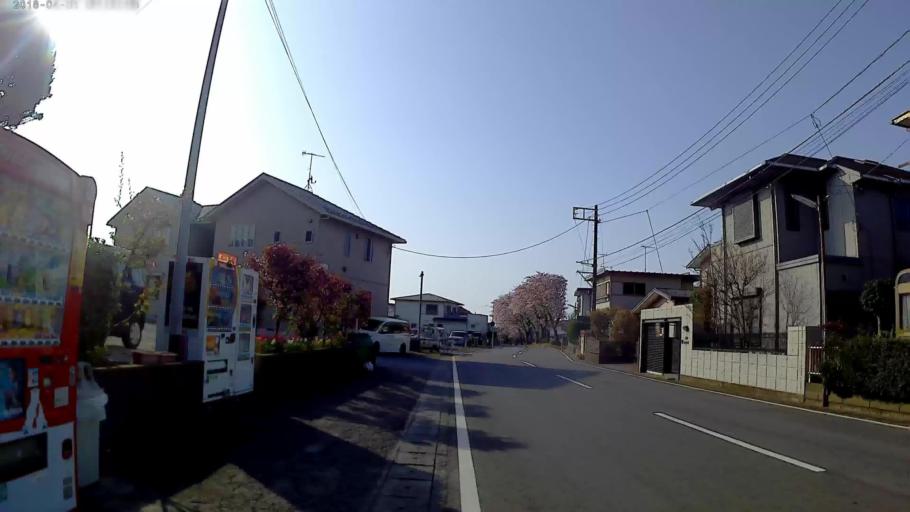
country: JP
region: Kanagawa
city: Atsugi
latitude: 35.4362
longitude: 139.4082
